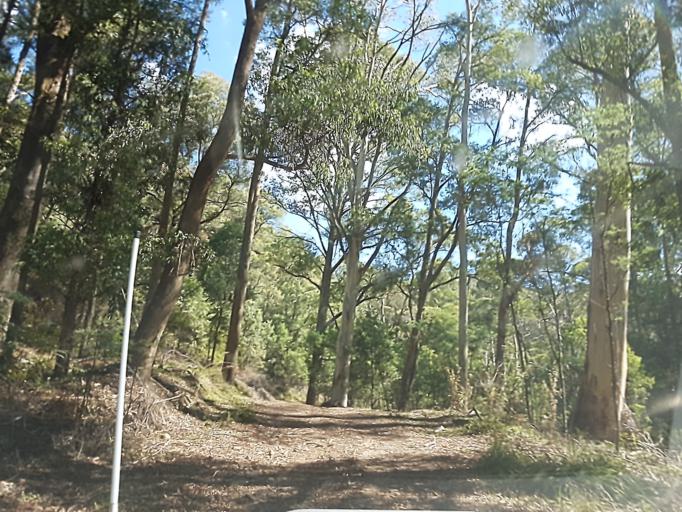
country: AU
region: Victoria
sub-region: Alpine
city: Mount Beauty
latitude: -36.8773
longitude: 147.0466
